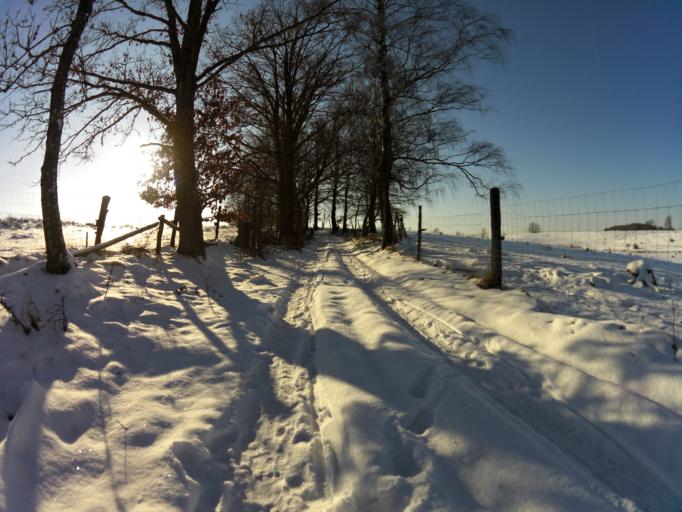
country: PL
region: West Pomeranian Voivodeship
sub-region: Powiat stargardzki
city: Dobrzany
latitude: 53.3844
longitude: 15.4856
